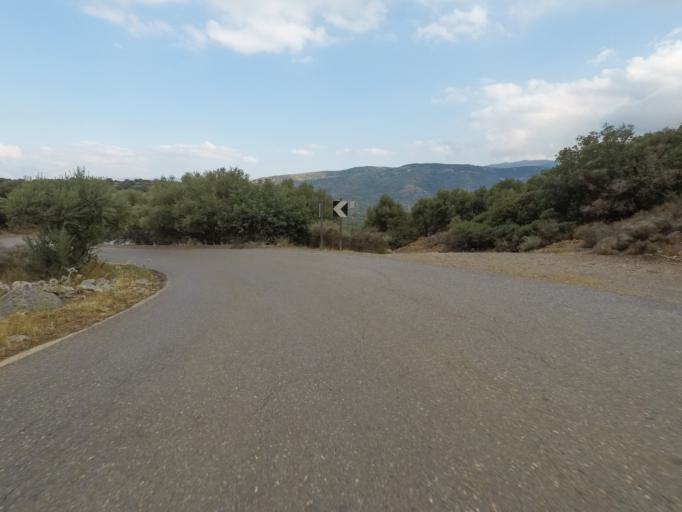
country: GR
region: Crete
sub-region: Nomos Lasithiou
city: Kritsa
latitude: 35.1679
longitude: 25.6547
